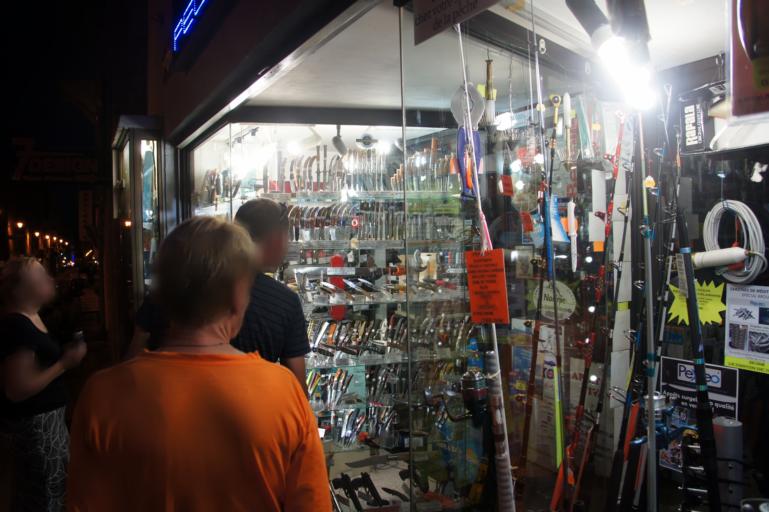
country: FR
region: Corsica
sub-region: Departement de la Corse-du-Sud
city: Propriano
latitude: 41.6763
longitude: 8.9079
